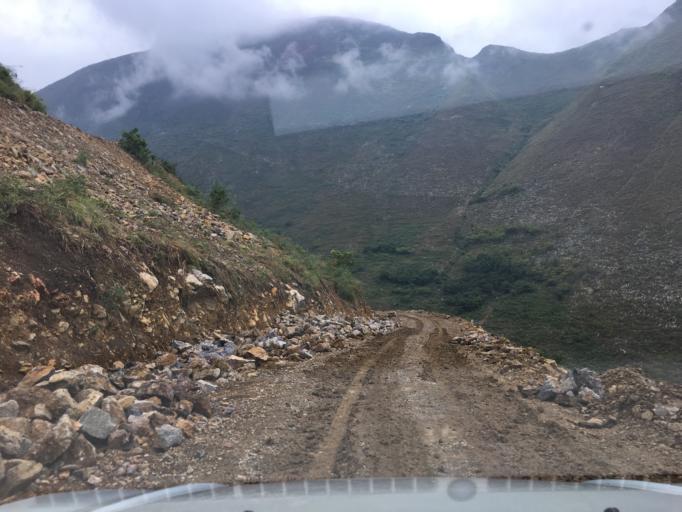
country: CN
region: Guizhou Sheng
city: Anshun
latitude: 25.9621
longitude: 105.2397
